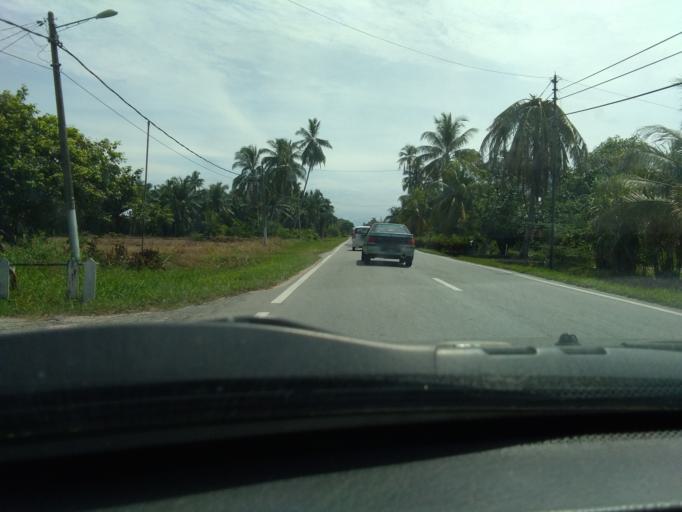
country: MY
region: Perak
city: Bagan Serai
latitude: 5.0280
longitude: 100.5570
